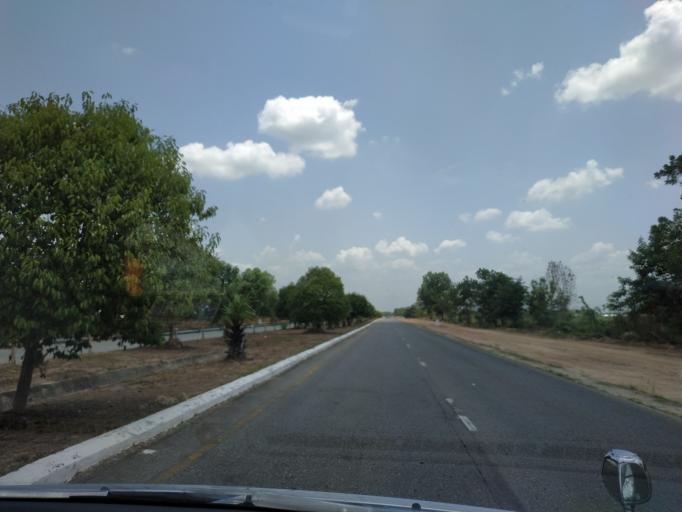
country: MM
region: Bago
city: Thanatpin
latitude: 17.1447
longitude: 96.1956
